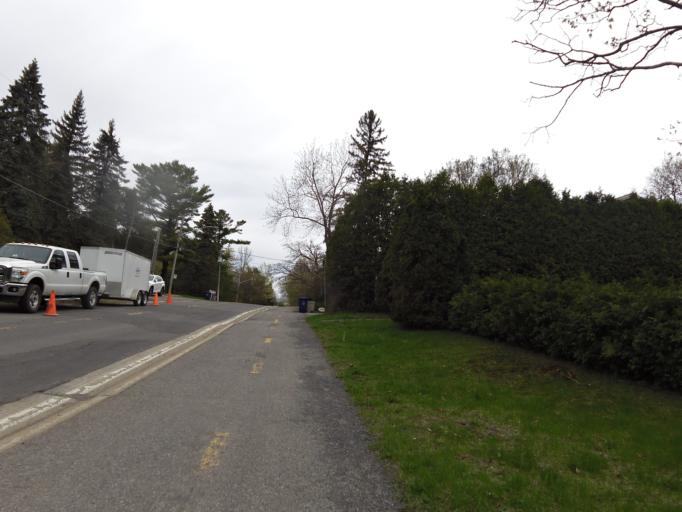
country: CA
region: Quebec
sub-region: Laurentides
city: Deux-Montagnes
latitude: 45.5230
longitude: -73.8725
